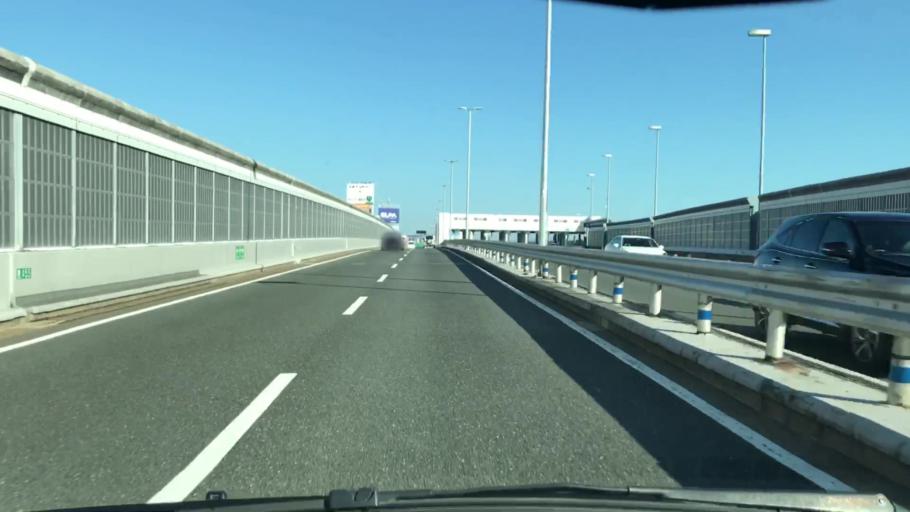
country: JP
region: Osaka
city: Toyonaka
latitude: 34.7825
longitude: 135.4531
